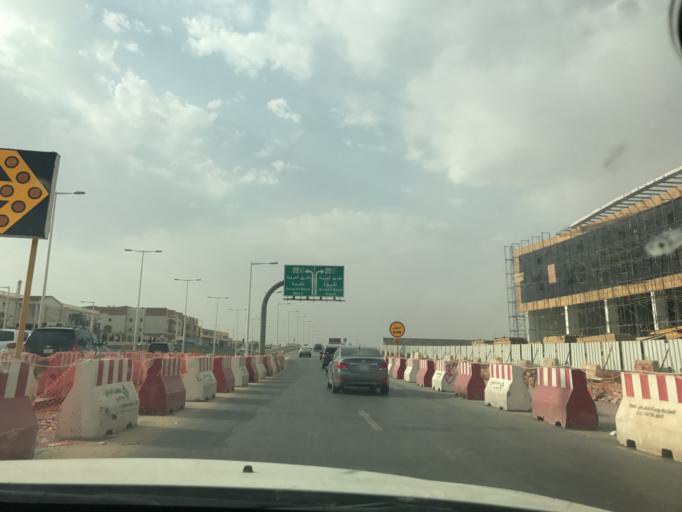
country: SA
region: Ar Riyad
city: Riyadh
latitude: 24.7177
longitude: 46.6951
